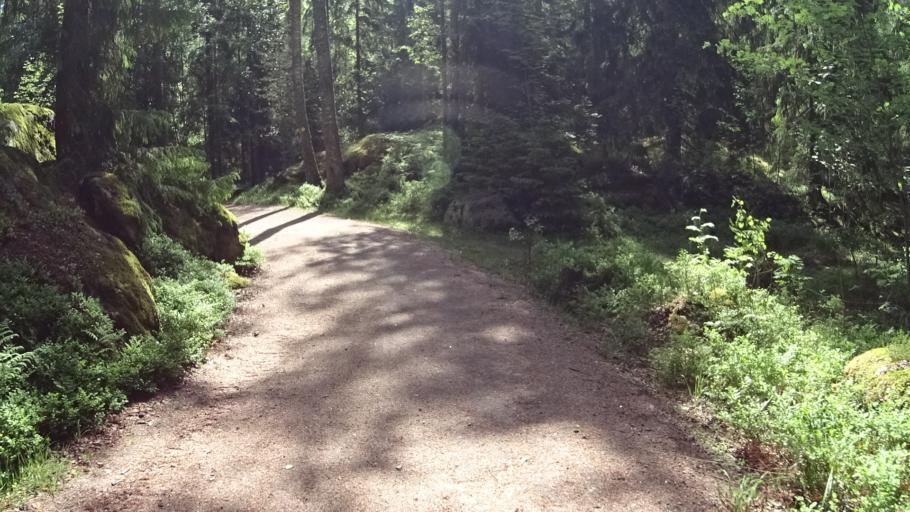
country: FI
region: Uusimaa
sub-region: Helsinki
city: Espoo
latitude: 60.3210
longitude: 24.6761
